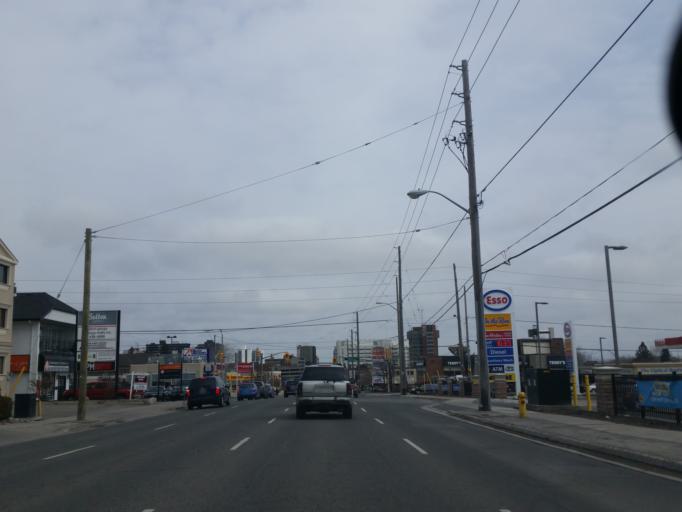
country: CA
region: Ontario
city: Oshawa
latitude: 43.8951
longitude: -78.8747
